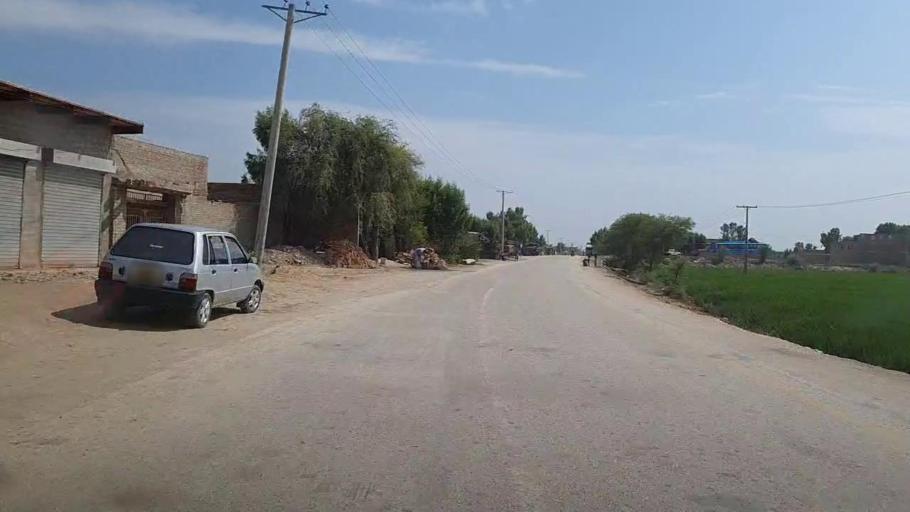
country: PK
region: Sindh
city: Thul
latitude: 28.2389
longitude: 68.7894
